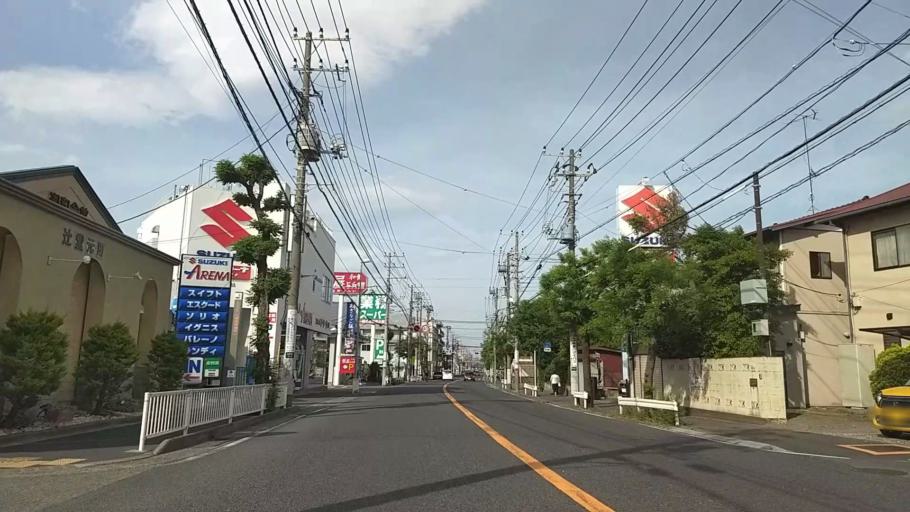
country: JP
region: Kanagawa
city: Fujisawa
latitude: 35.3304
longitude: 139.4581
